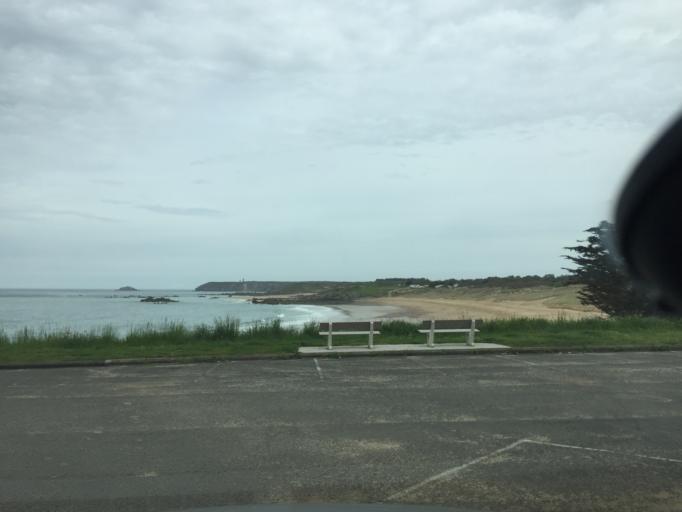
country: FR
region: Brittany
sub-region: Departement des Cotes-d'Armor
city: Plurien
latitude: 48.6546
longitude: -2.3657
